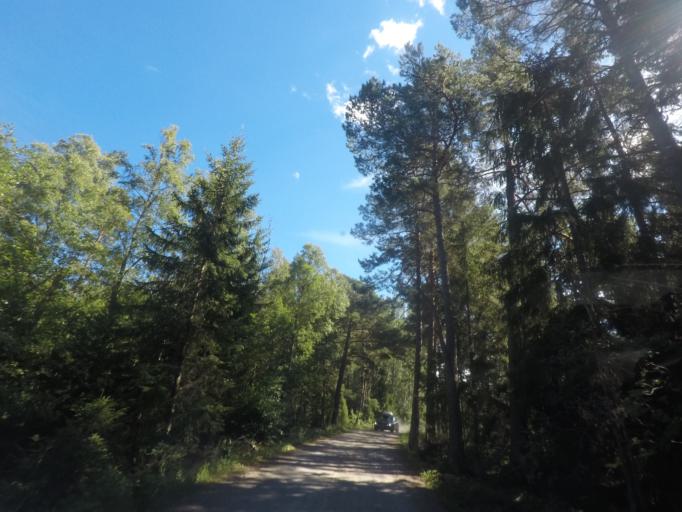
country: SE
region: Stockholm
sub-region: Norrtalje Kommun
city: Arno
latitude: 60.2140
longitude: 18.7302
